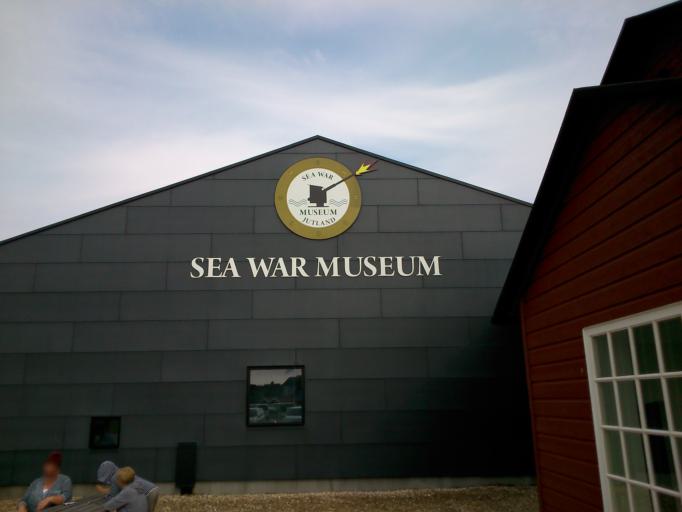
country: DK
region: Central Jutland
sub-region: Lemvig Kommune
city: Thyboron
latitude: 56.7064
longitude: 8.2154
